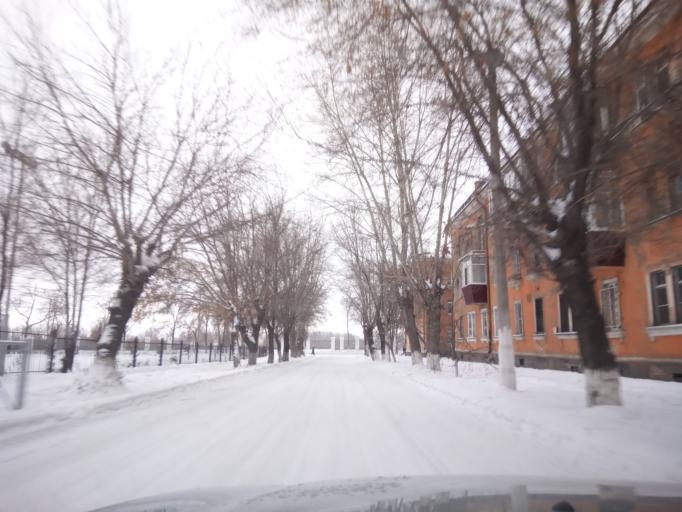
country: RU
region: Orenburg
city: Novotroitsk
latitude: 51.1965
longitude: 58.3269
